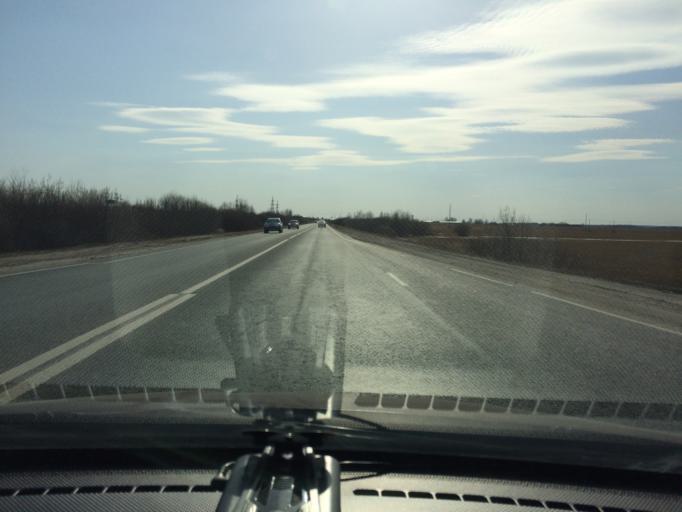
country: RU
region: Mariy-El
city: Yoshkar-Ola
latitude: 56.6760
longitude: 48.0146
